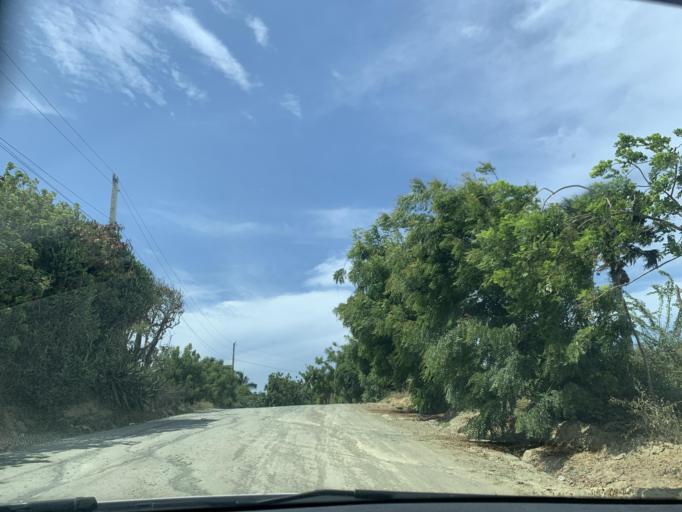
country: DO
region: Puerto Plata
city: Imbert
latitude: 19.8711
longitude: -70.8215
